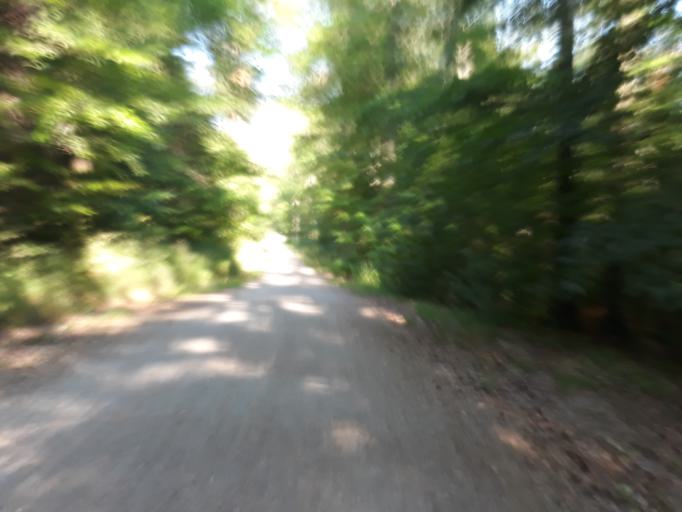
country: DE
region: Baden-Wuerttemberg
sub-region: Regierungsbezirk Stuttgart
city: Schonaich
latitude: 48.6769
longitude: 9.0411
